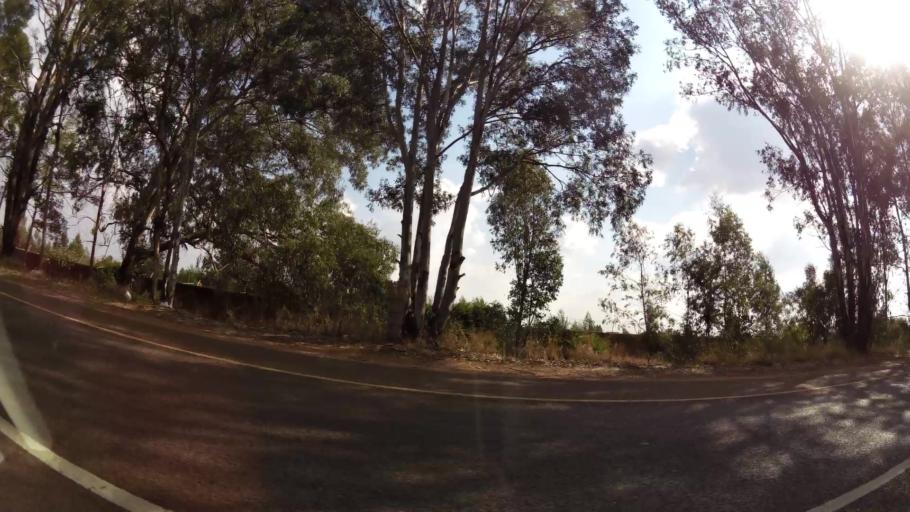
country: ZA
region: Gauteng
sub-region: City of Tshwane Metropolitan Municipality
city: Centurion
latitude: -25.8294
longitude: 28.2347
